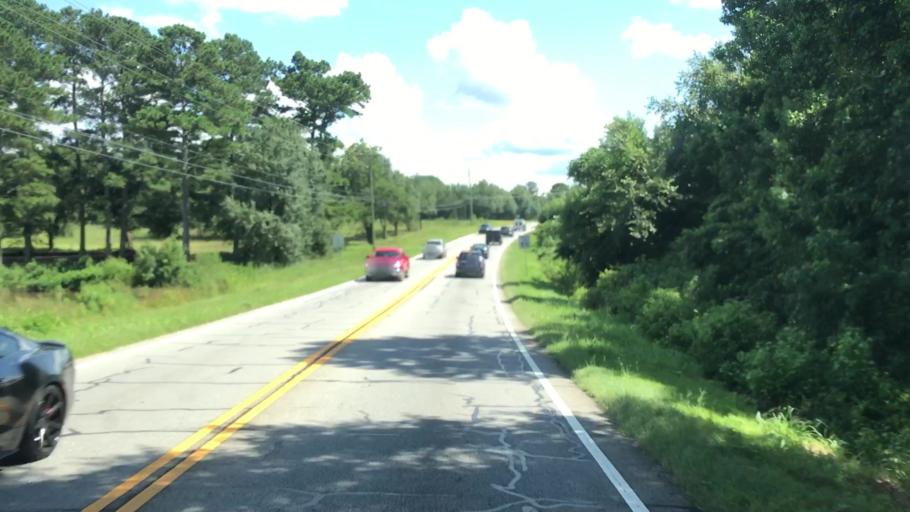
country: US
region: Georgia
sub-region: Walton County
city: Loganville
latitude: 33.8120
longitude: -83.8742
